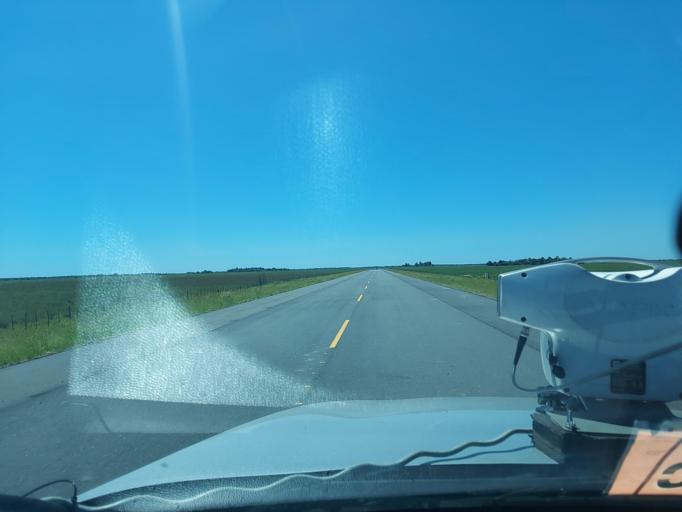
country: PY
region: Neembucu
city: Pilar
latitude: -26.8270
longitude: -58.2409
